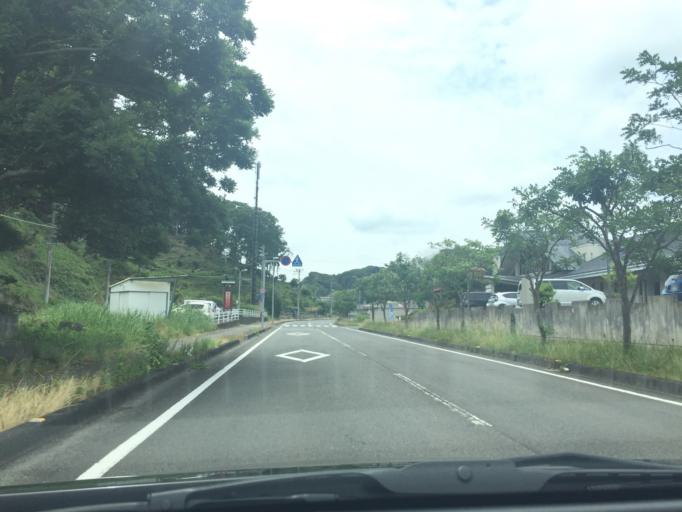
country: JP
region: Shizuoka
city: Shimoda
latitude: 34.6488
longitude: 138.8610
